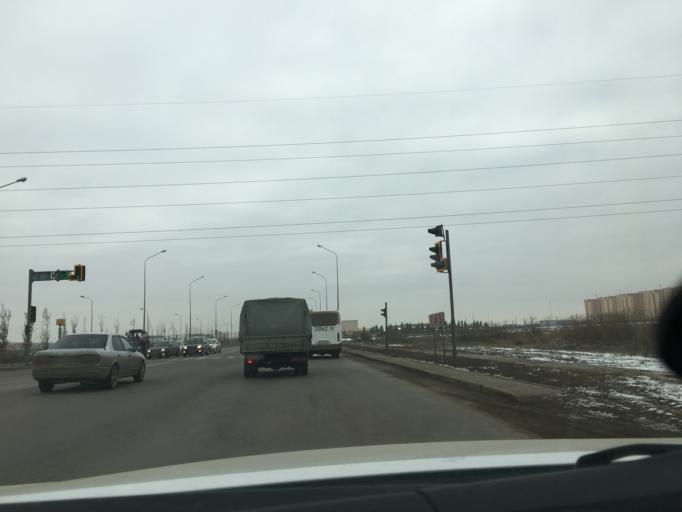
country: KZ
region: Astana Qalasy
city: Astana
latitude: 51.1611
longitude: 71.5164
